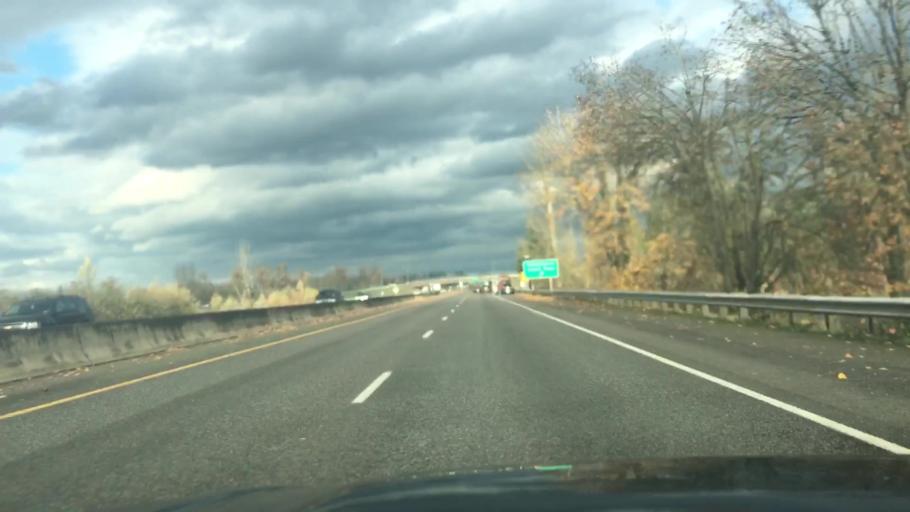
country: US
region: Oregon
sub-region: Lane County
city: Eugene
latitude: 44.0807
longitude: -123.1040
